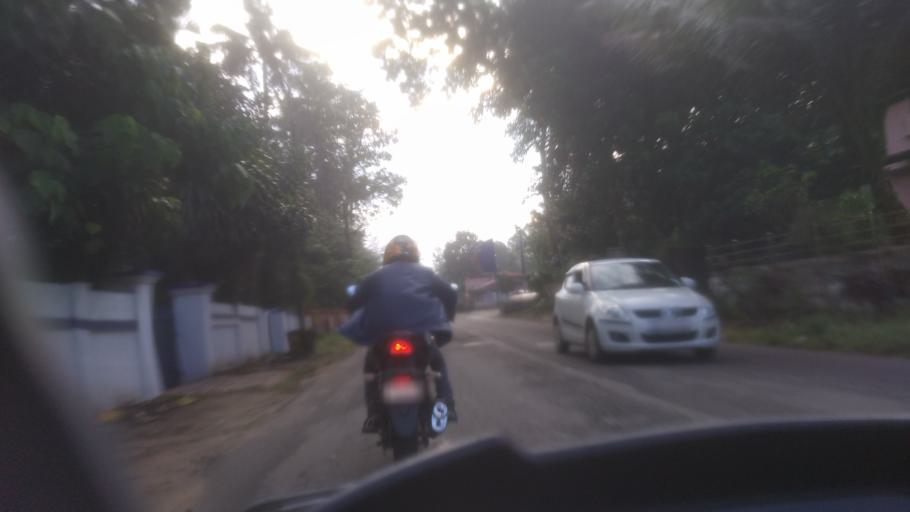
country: IN
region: Kerala
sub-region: Ernakulam
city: Perumpavur
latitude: 10.1049
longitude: 76.5375
